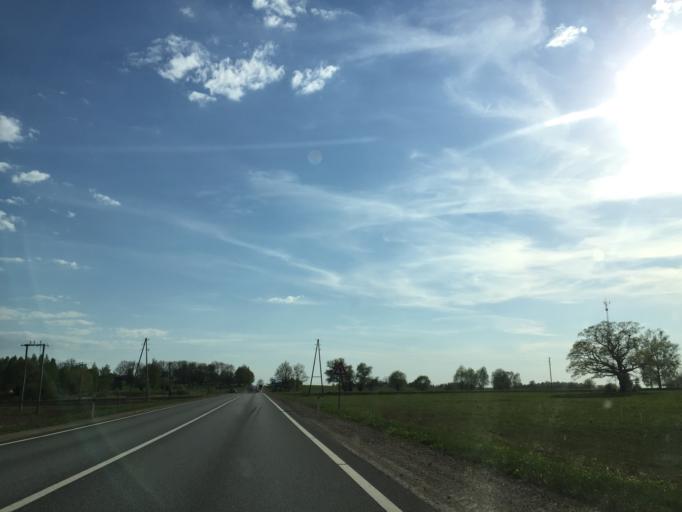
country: LV
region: Sigulda
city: Sigulda
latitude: 57.2647
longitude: 24.8787
